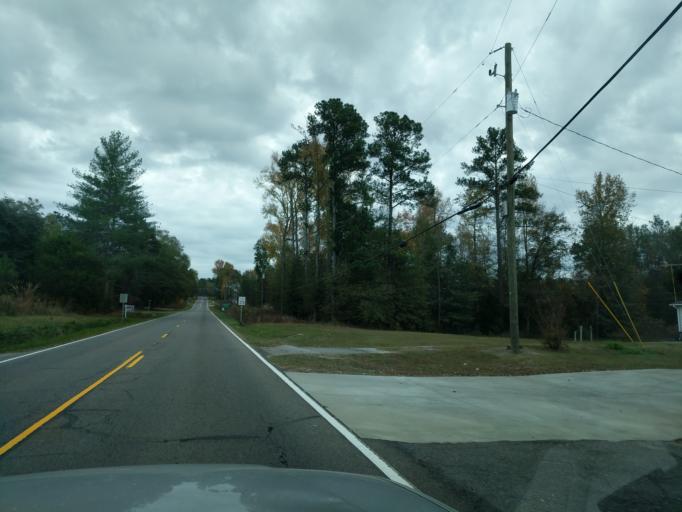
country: US
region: South Carolina
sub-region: Lexington County
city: Batesburg
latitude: 33.9165
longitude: -81.5685
